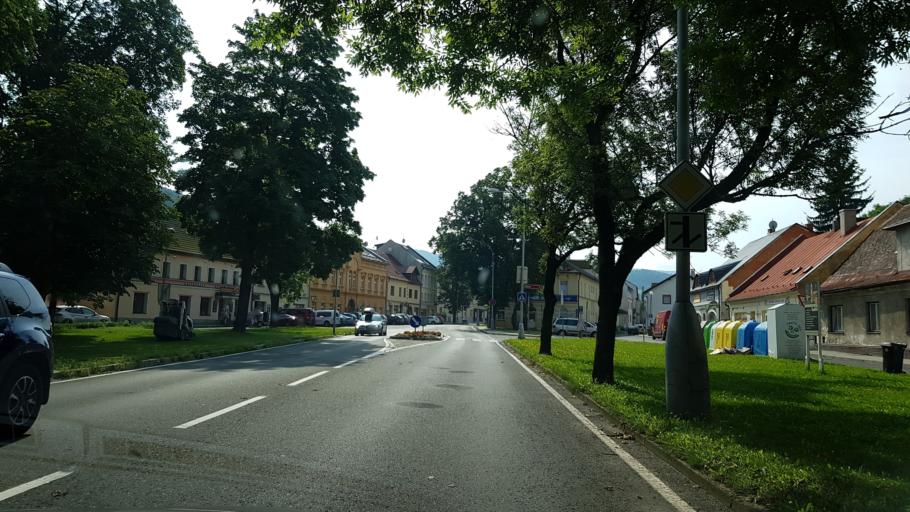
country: CZ
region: Olomoucky
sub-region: Okres Jesenik
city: Jesenik
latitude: 50.2271
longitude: 17.2050
